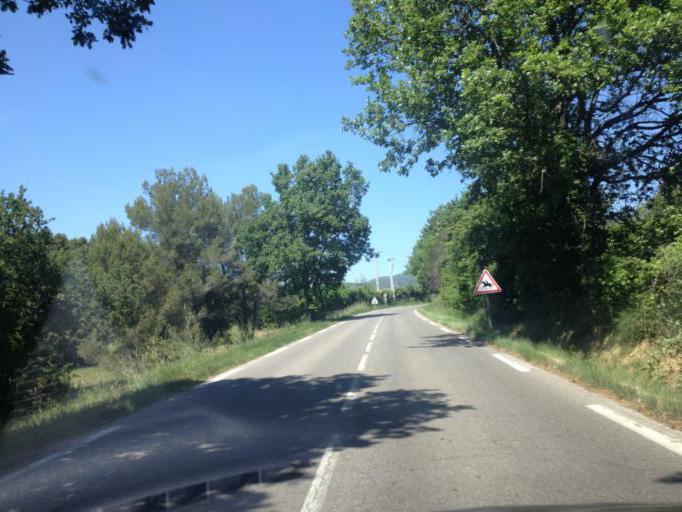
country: FR
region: Provence-Alpes-Cote d'Azur
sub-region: Departement du Vaucluse
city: Lourmarin
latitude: 43.7498
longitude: 5.3639
